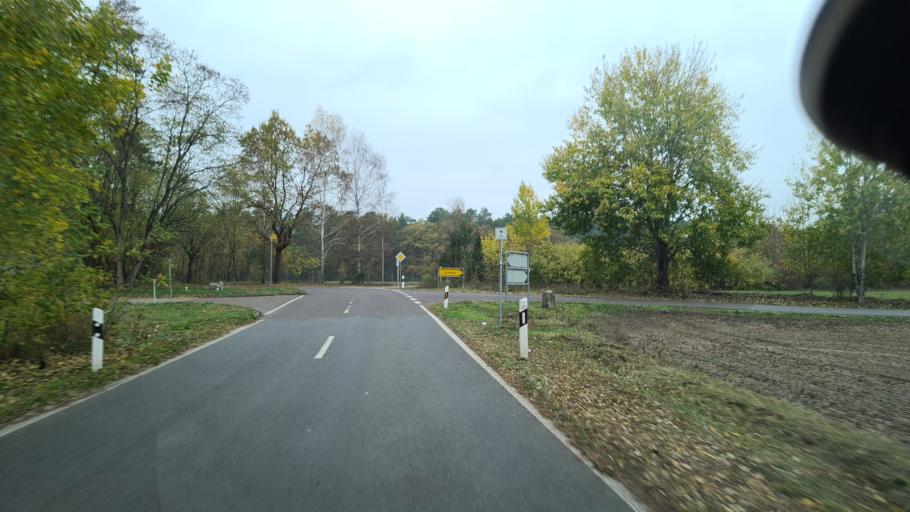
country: DE
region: Brandenburg
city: Lindow
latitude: 52.9596
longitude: 13.0021
